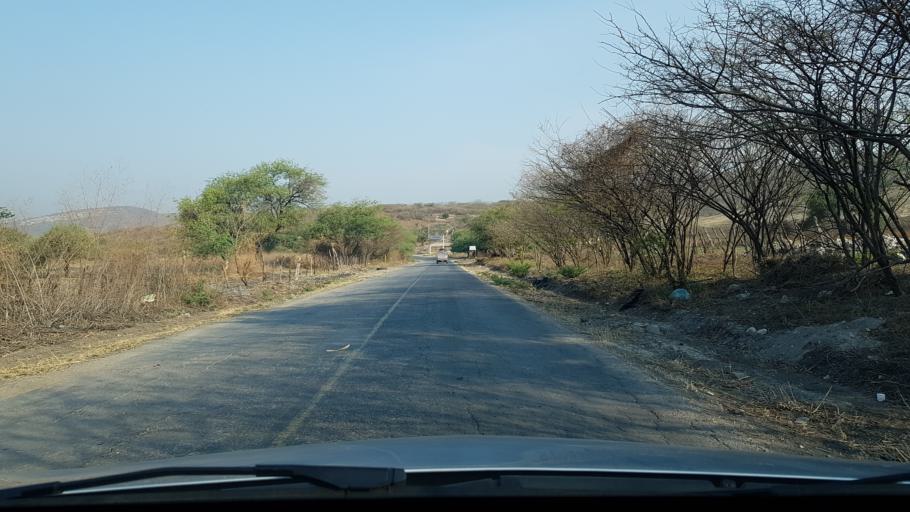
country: MX
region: Morelos
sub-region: Tlaltizapan de Zapata
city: Colonia Palo Prieto (Chipitongo)
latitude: 18.6900
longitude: -99.0949
